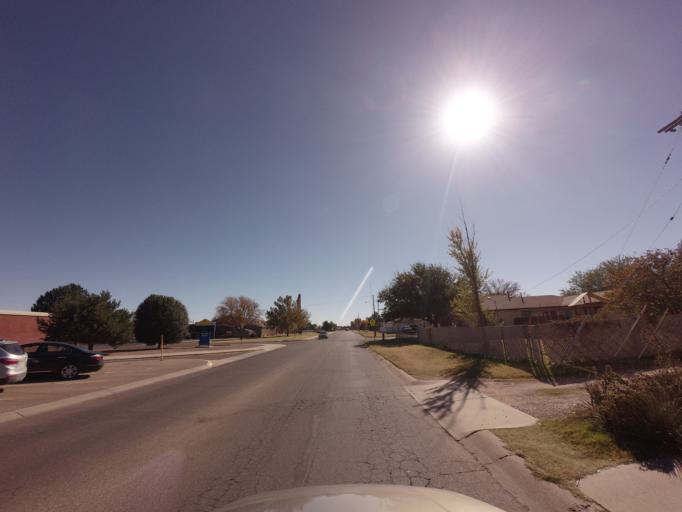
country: US
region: New Mexico
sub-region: Curry County
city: Clovis
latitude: 34.4259
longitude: -103.2070
